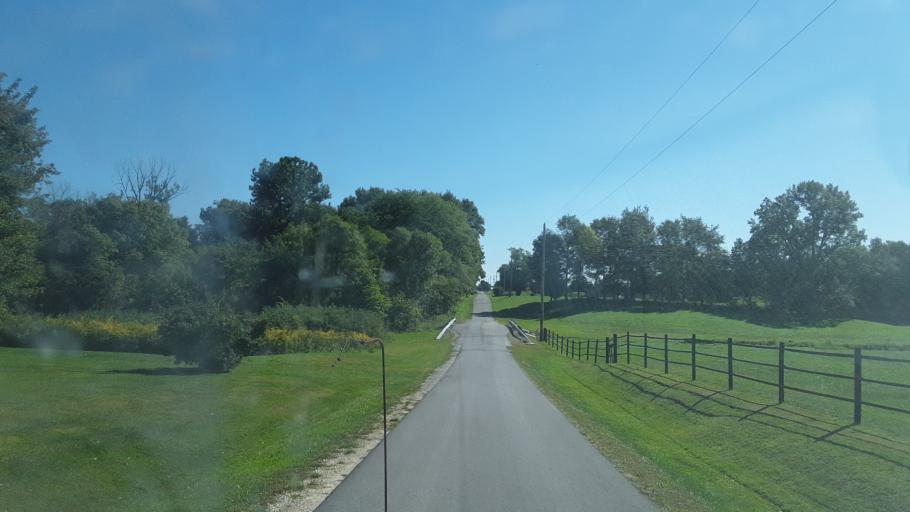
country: US
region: Ohio
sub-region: Wyandot County
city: Upper Sandusky
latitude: 40.9348
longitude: -83.2247
